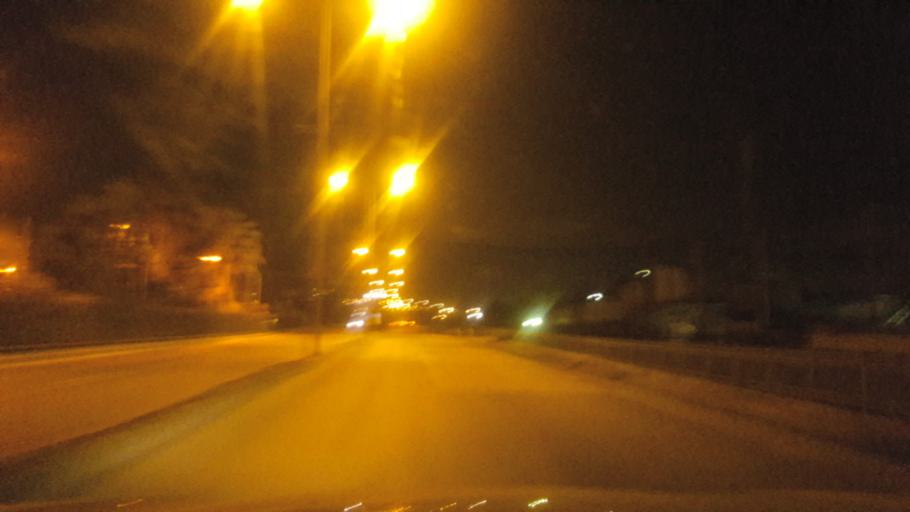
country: TR
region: Kocaeli
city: Tavsanli
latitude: 40.7833
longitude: 29.5298
